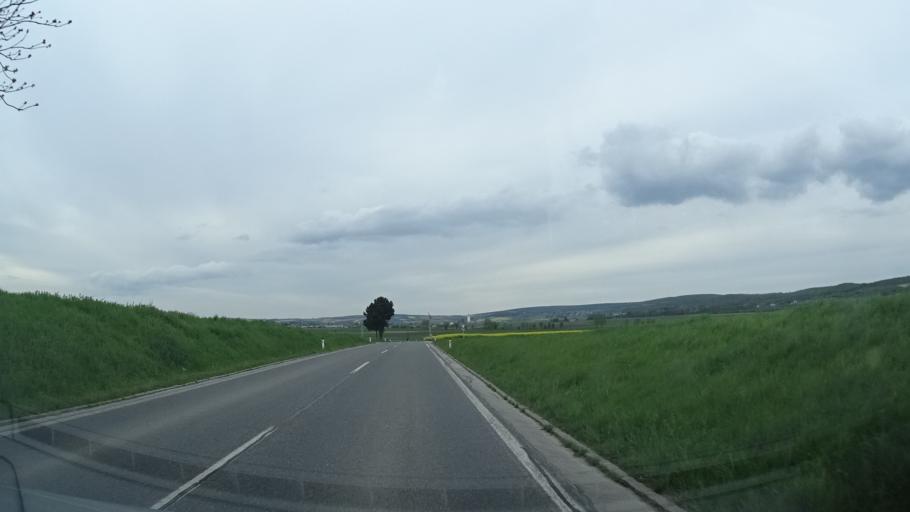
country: AT
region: Lower Austria
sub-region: Politischer Bezirk Korneuburg
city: Harmannsdorf
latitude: 48.3703
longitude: 16.3589
